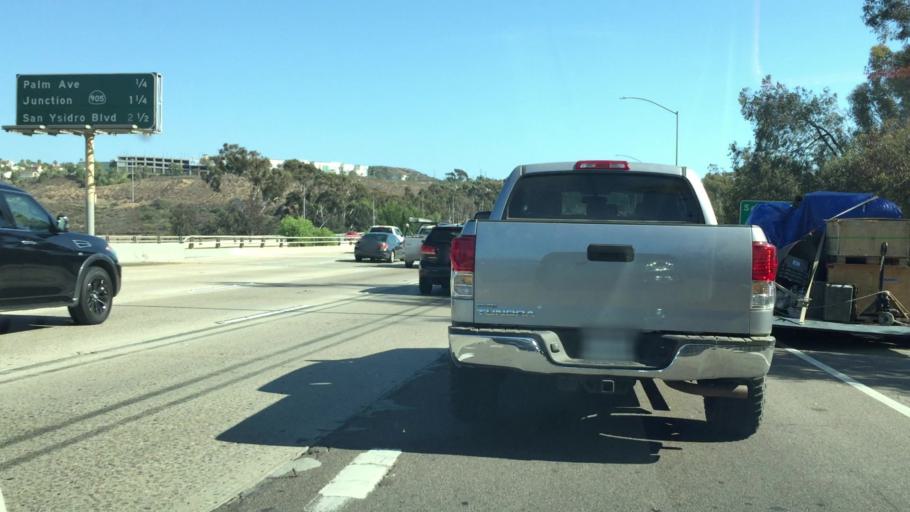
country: US
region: California
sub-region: San Diego County
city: Bonita
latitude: 32.5916
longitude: -117.0366
